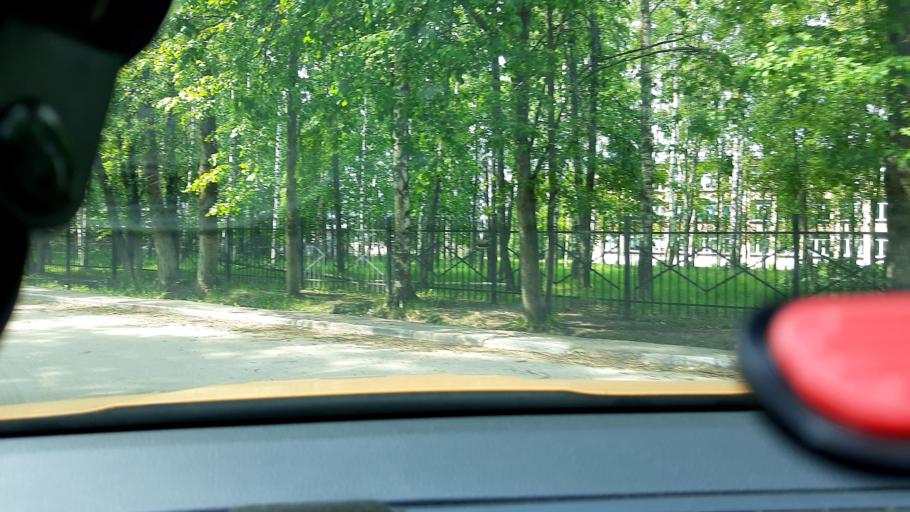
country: RU
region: Moskovskaya
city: Kubinka
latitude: 55.5640
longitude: 36.7036
